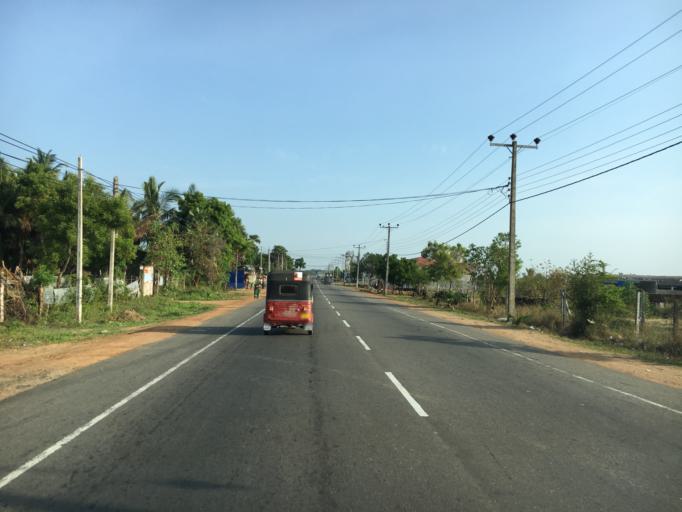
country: LK
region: Eastern Province
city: Eravur Town
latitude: 7.9298
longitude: 81.5125
